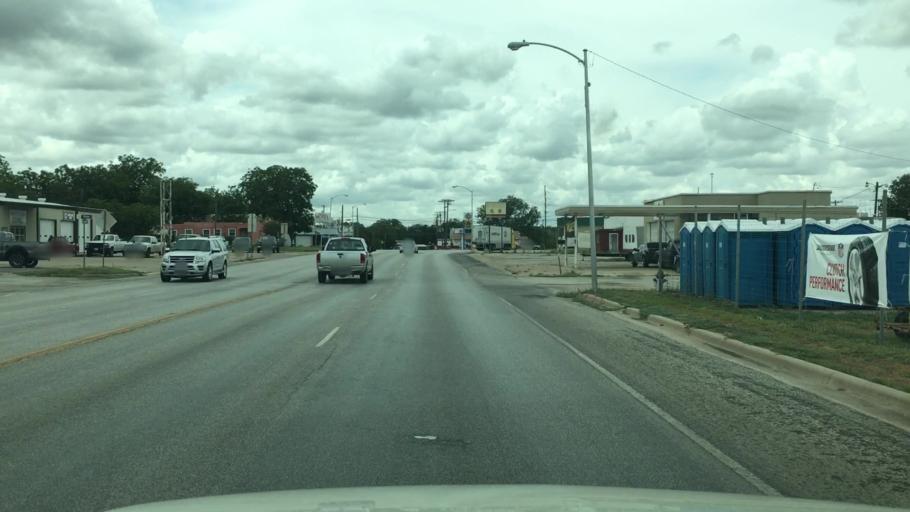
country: US
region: Texas
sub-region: McCulloch County
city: Brady
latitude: 31.1349
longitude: -99.3380
